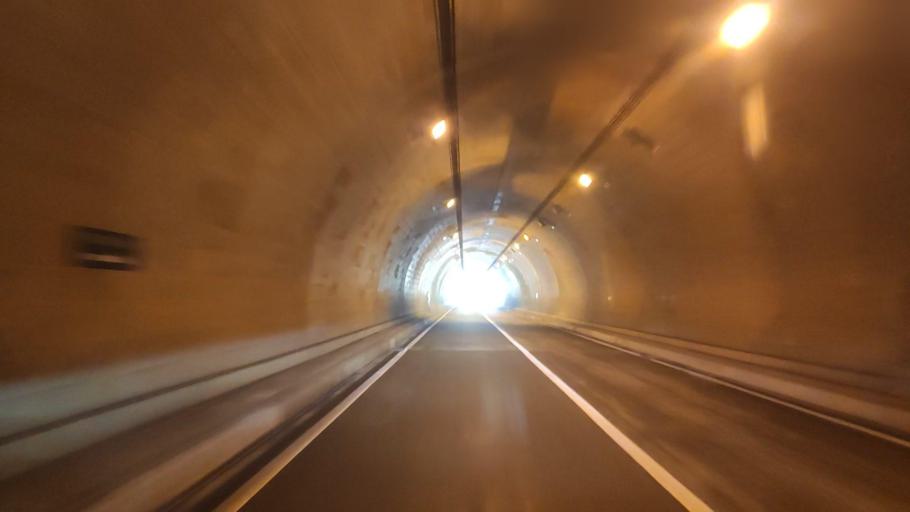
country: JP
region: Wakayama
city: Shingu
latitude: 33.9210
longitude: 135.9142
